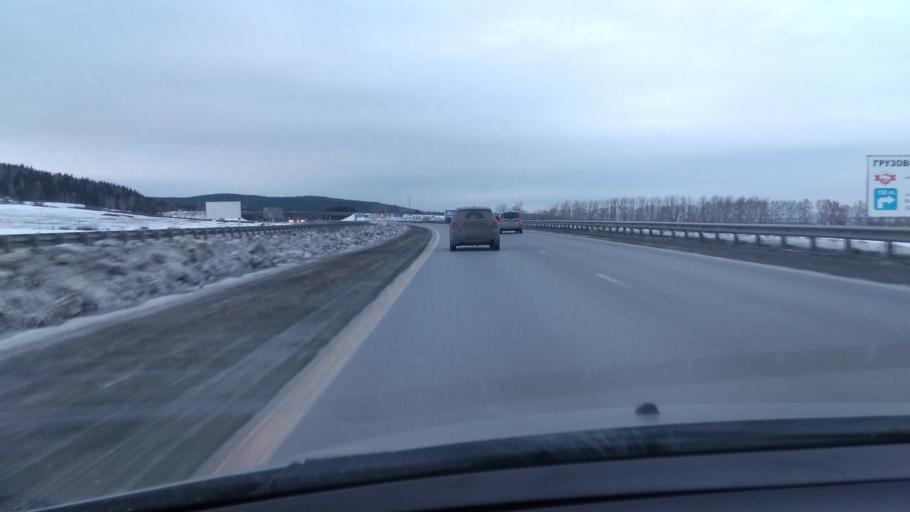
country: RU
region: Sverdlovsk
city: Aramil
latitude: 56.6906
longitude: 60.7641
